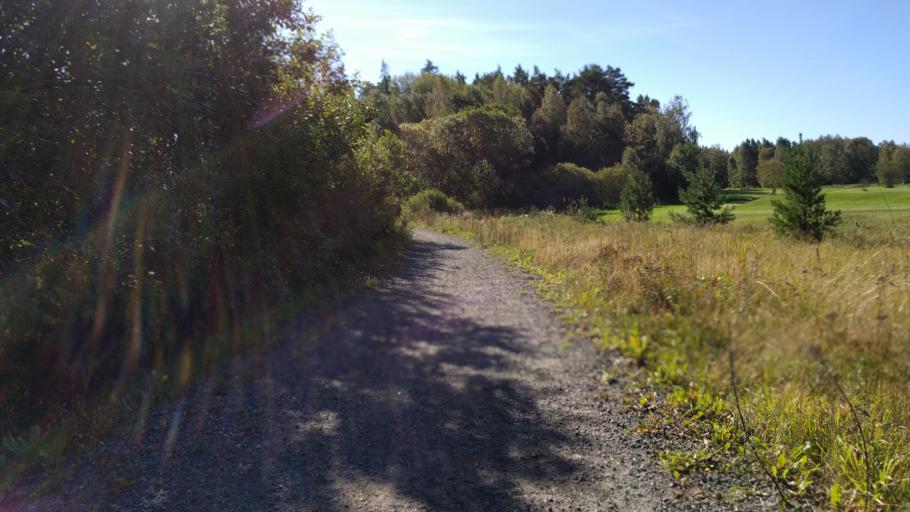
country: SE
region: Stockholm
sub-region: Vallentuna Kommun
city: Vallentuna
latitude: 59.4977
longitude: 18.1007
